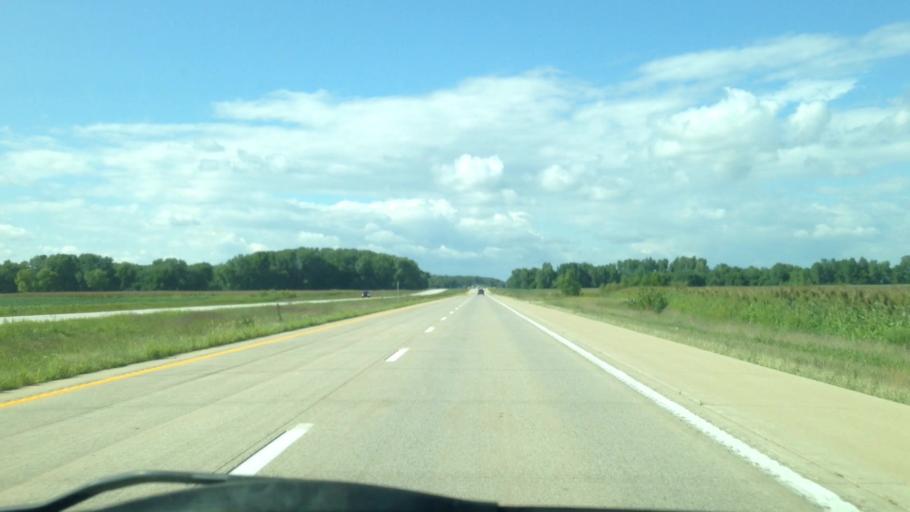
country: US
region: Illinois
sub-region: Hancock County
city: Warsaw
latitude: 40.2913
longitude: -91.5684
